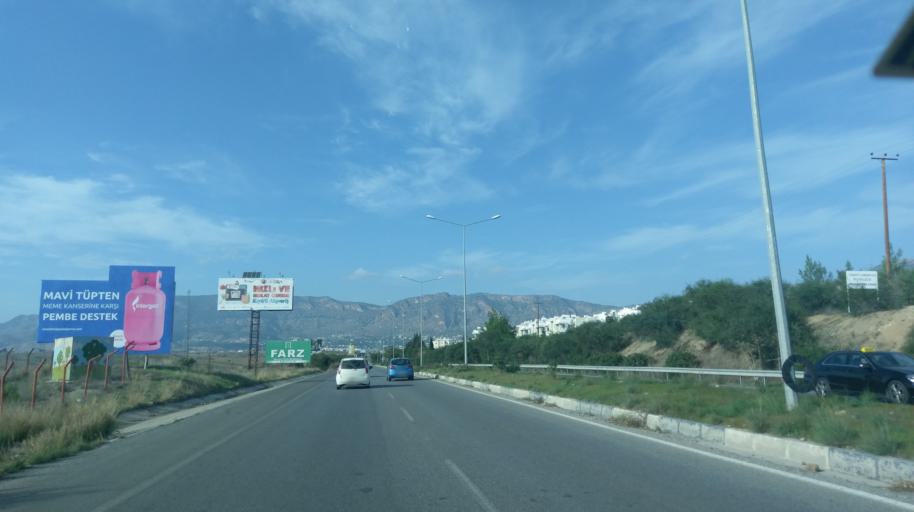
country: CY
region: Keryneia
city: Kyrenia
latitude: 35.2532
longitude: 33.3018
